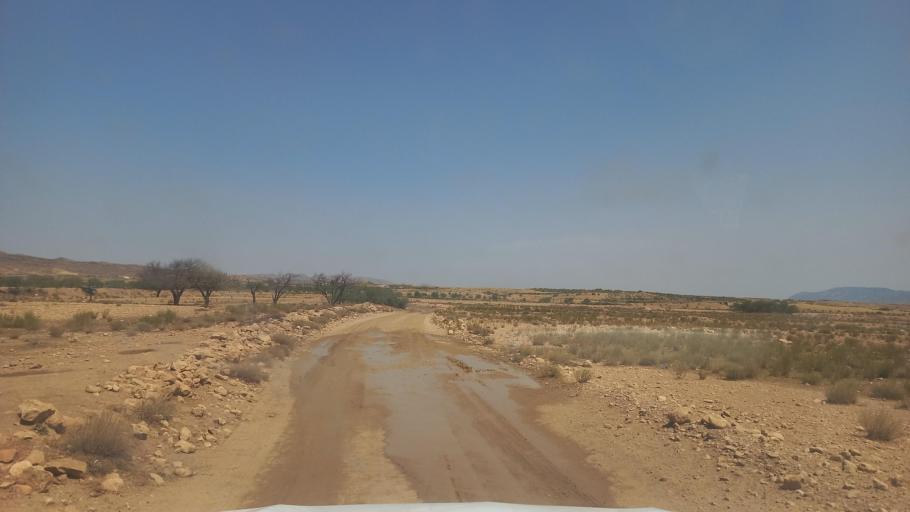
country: TN
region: Al Qasrayn
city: Kasserine
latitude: 35.2897
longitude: 8.9522
